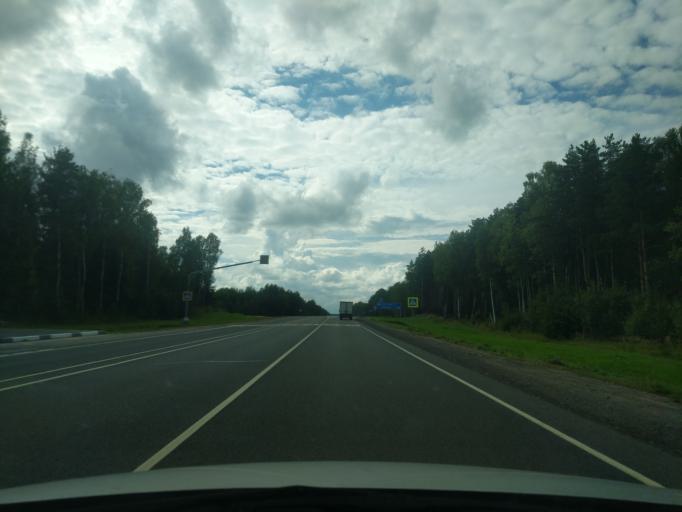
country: RU
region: Jaroslavl
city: Levashevo
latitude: 57.6398
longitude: 40.4663
